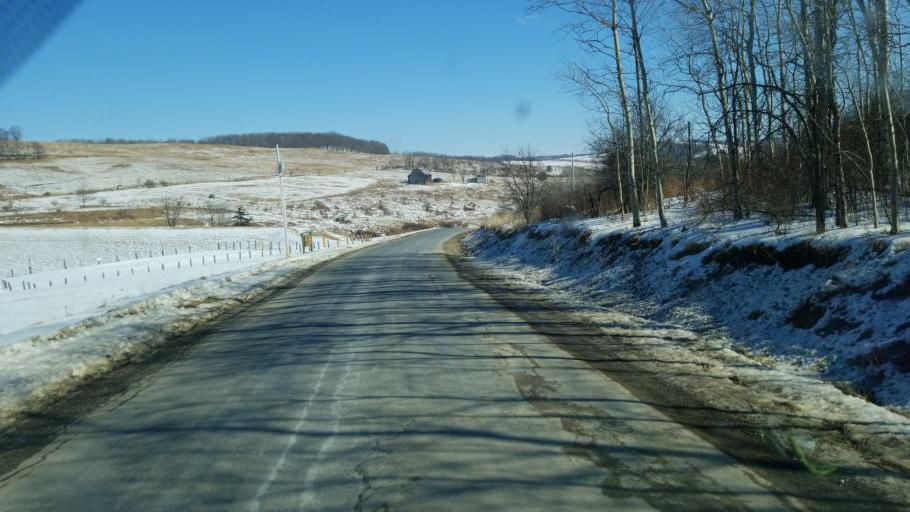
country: US
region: Pennsylvania
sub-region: Tioga County
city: Westfield
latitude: 41.9944
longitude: -77.6507
